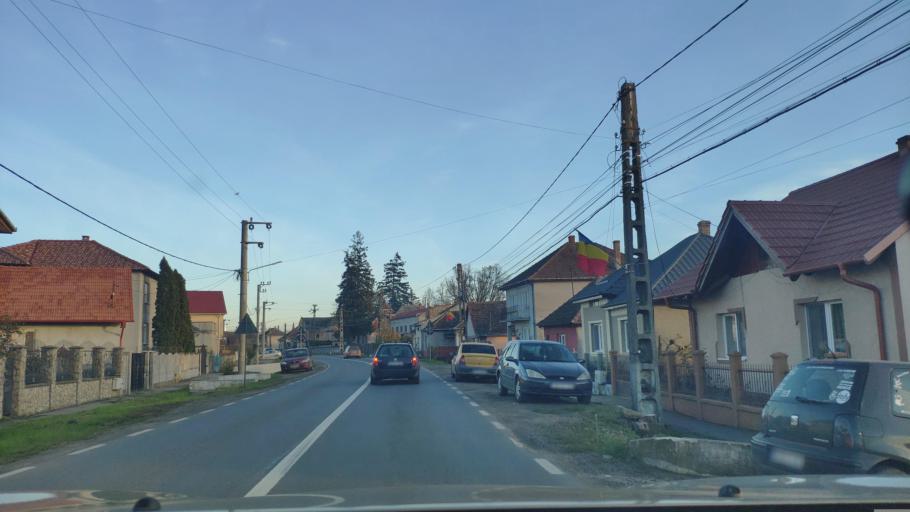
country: RO
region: Satu Mare
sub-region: Comuna Odoreu
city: Odoreu
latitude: 47.7960
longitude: 22.9853
